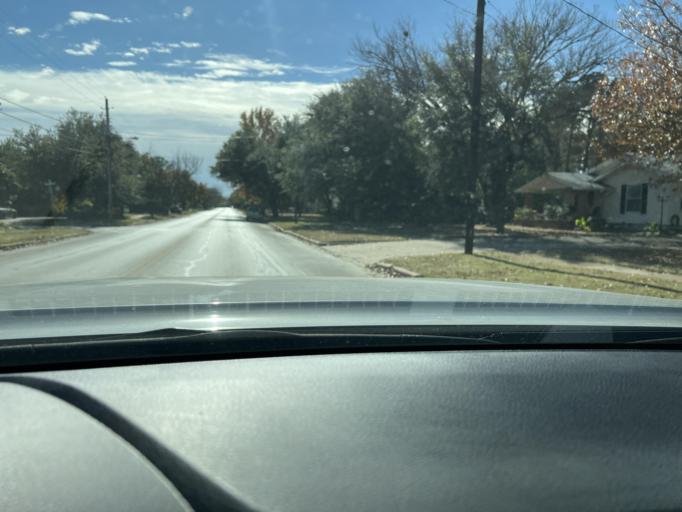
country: US
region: Texas
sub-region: Eastland County
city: Eastland
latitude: 32.3941
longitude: -98.8181
